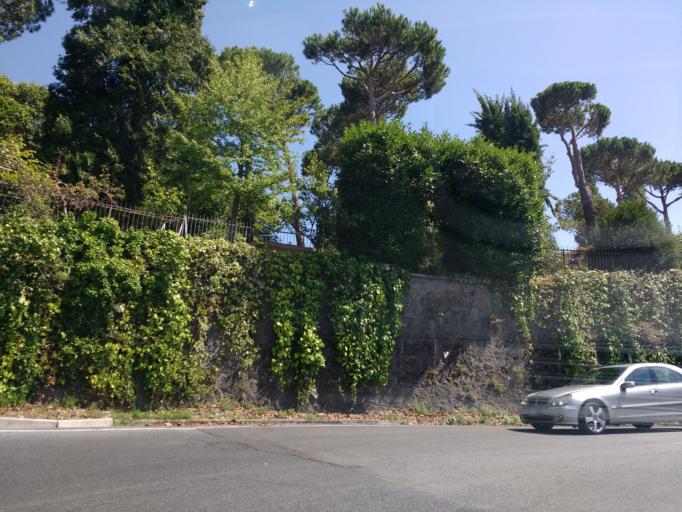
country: IT
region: Latium
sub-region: Citta metropolitana di Roma Capitale
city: Rocca di Papa
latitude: 41.7674
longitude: 12.7113
